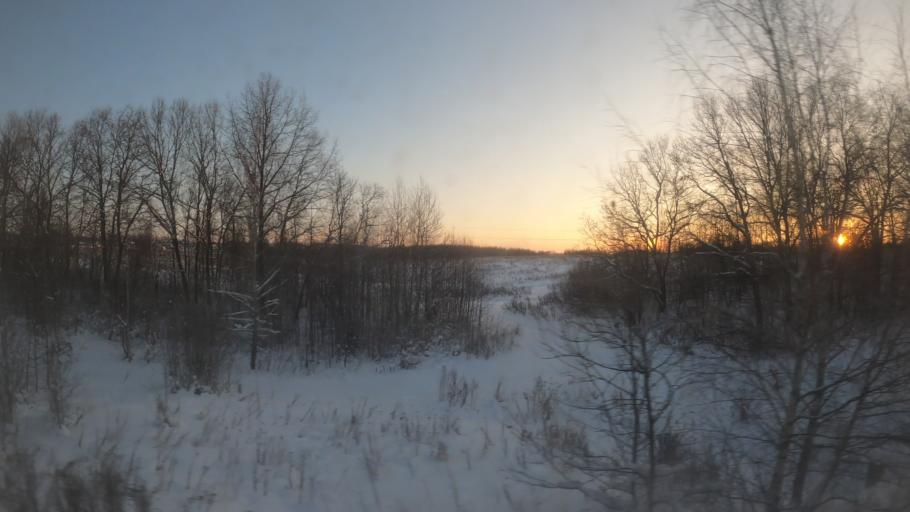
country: RU
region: Moskovskaya
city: Dedenevo
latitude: 56.2636
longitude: 37.5119
